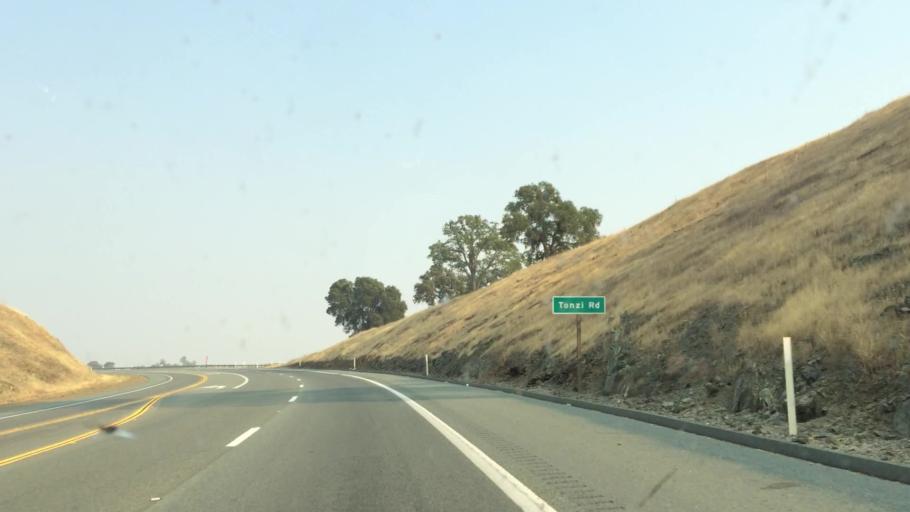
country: US
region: California
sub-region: Amador County
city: Sutter Creek
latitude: 38.4079
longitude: -120.8338
